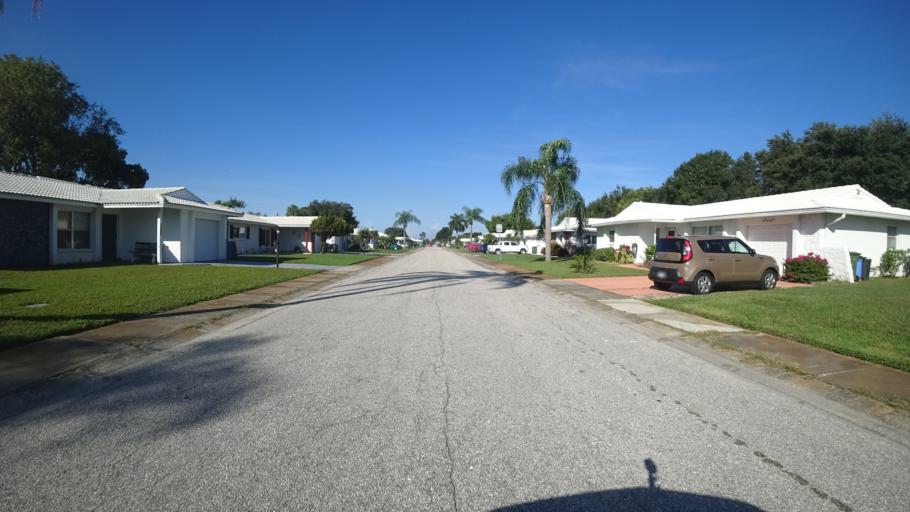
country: US
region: Florida
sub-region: Manatee County
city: Ellenton
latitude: 27.4970
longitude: -82.5091
